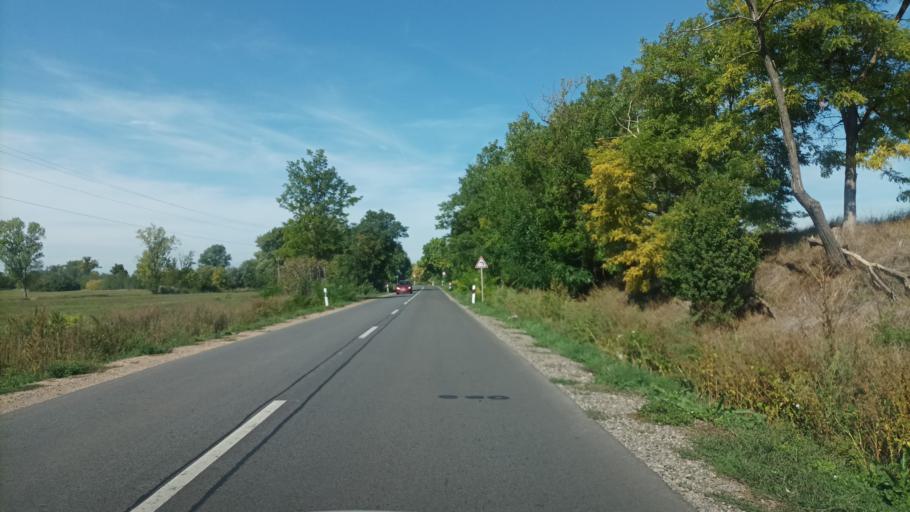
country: HU
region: Pest
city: Zsambok
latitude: 47.5506
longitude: 19.5979
